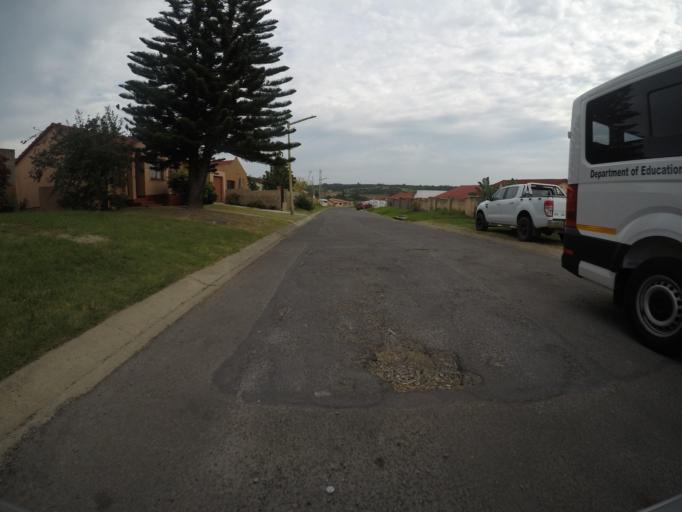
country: ZA
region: Eastern Cape
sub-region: Buffalo City Metropolitan Municipality
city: East London
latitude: -32.9768
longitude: 27.8610
